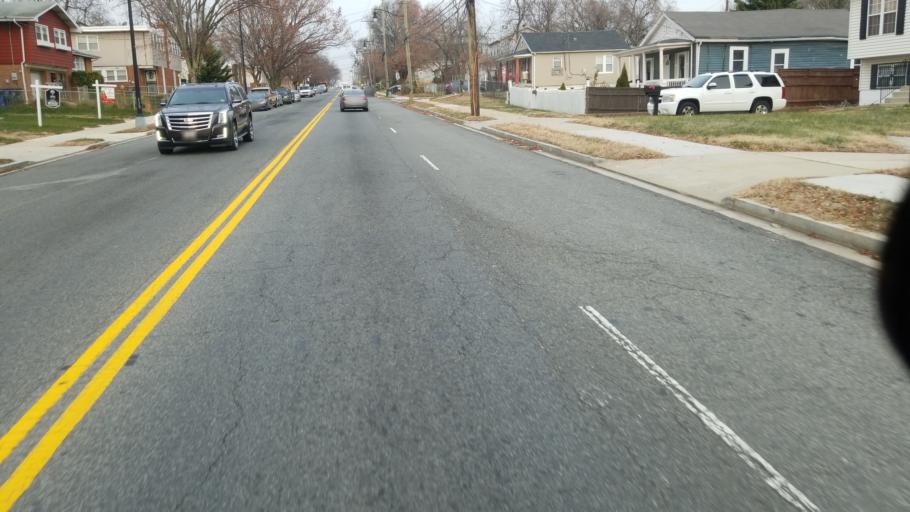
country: US
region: Maryland
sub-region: Prince George's County
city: Fairmount Heights
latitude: 38.8999
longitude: -76.9182
